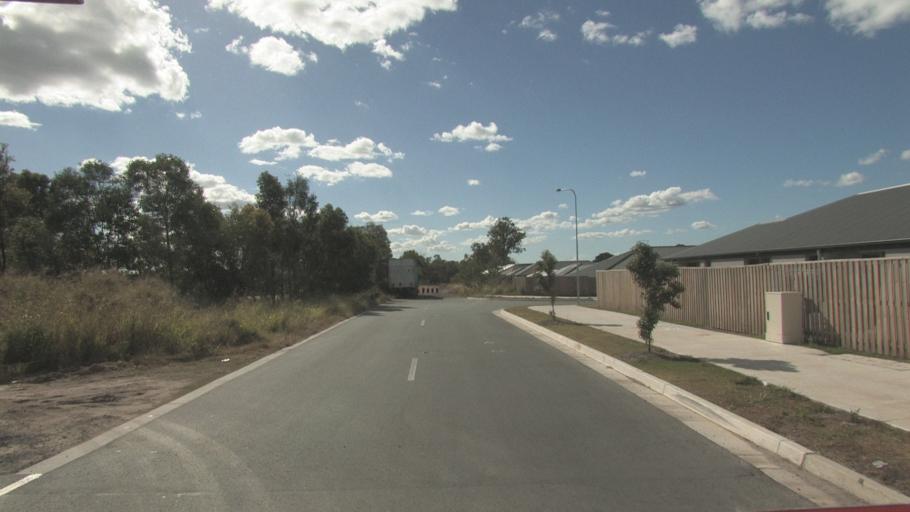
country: AU
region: Queensland
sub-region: Logan
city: Logan Reserve
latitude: -27.7144
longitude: 153.0839
